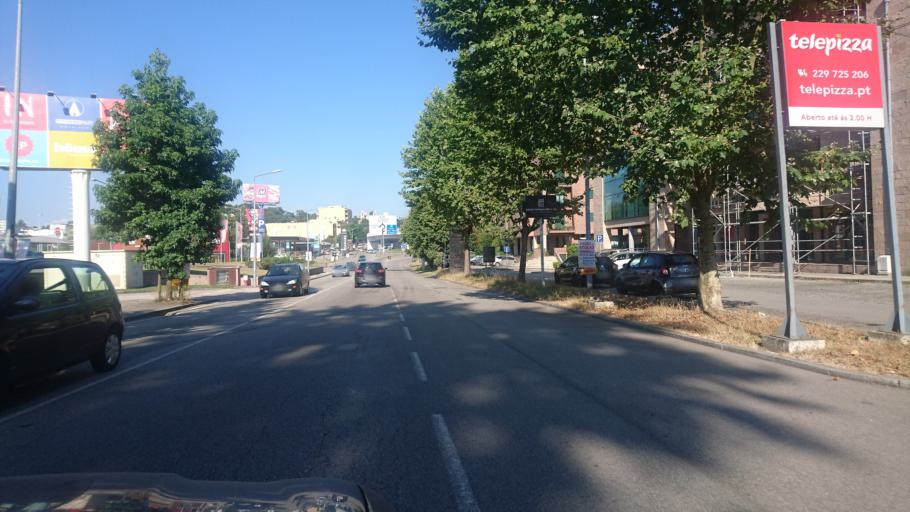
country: PT
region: Porto
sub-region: Gondomar
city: Baguim do Monte
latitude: 41.2049
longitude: -8.5507
